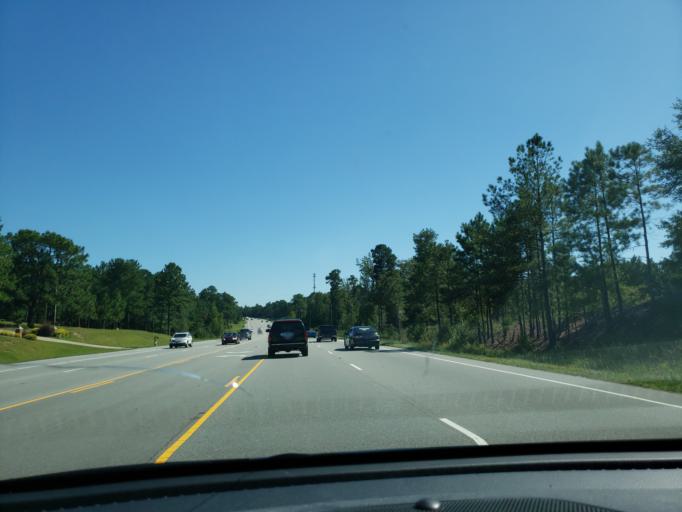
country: US
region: North Carolina
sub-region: Lee County
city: Broadway
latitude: 35.3513
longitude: -79.1087
